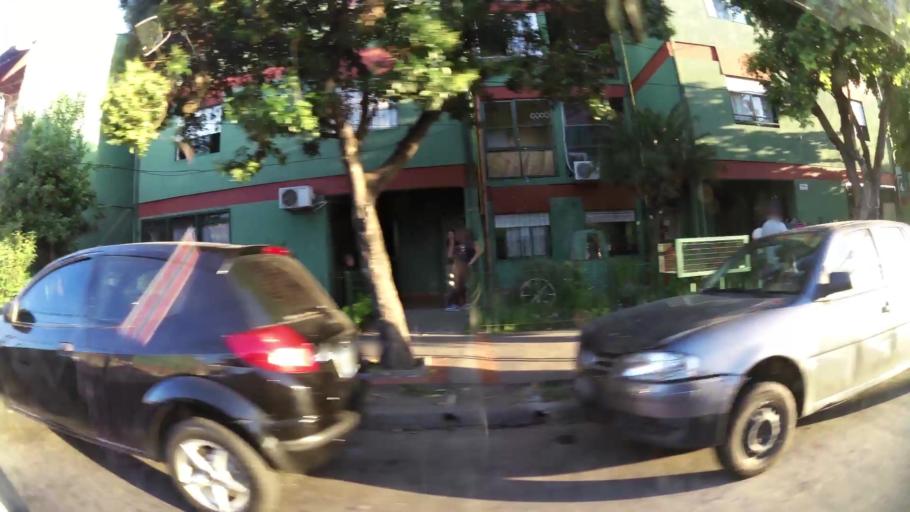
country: AR
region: Buenos Aires
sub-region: Partido de General San Martin
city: General San Martin
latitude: -34.5549
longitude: -58.5191
